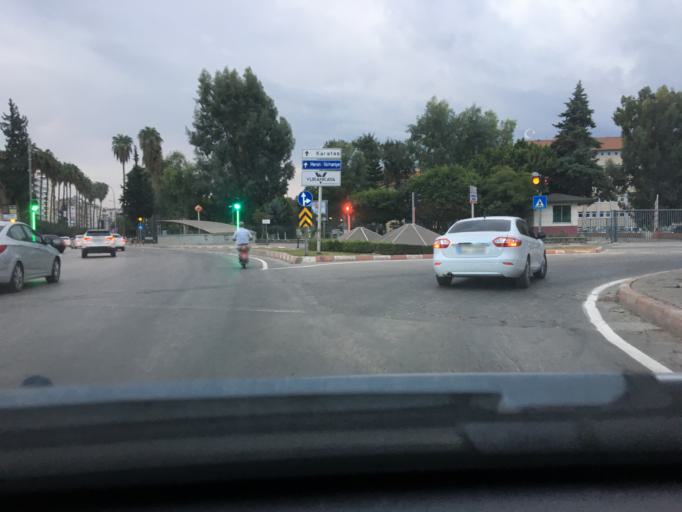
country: TR
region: Adana
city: Adana
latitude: 37.0019
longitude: 35.3133
